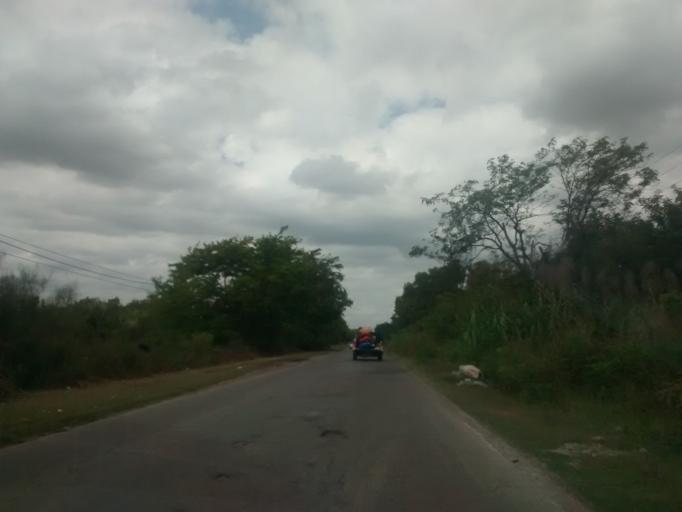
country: AR
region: Buenos Aires
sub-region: Partido de La Plata
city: La Plata
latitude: -34.9790
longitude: -57.9329
